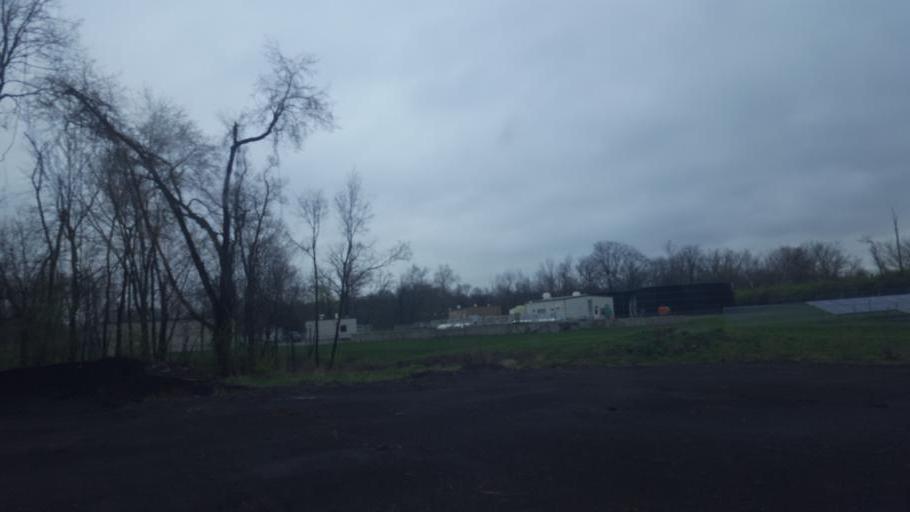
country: US
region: Ohio
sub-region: Morrow County
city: Mount Gilead
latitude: 40.5396
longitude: -82.8418
